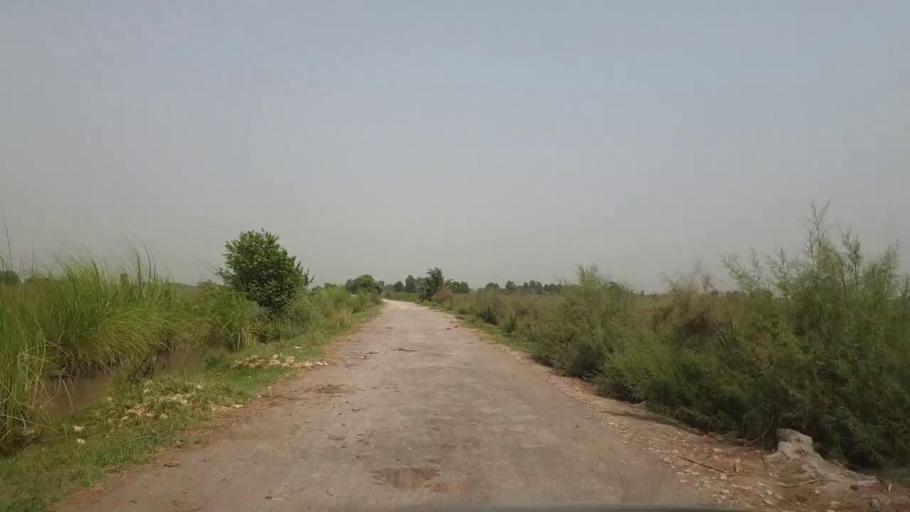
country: PK
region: Sindh
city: Gambat
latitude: 27.4500
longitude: 68.4431
